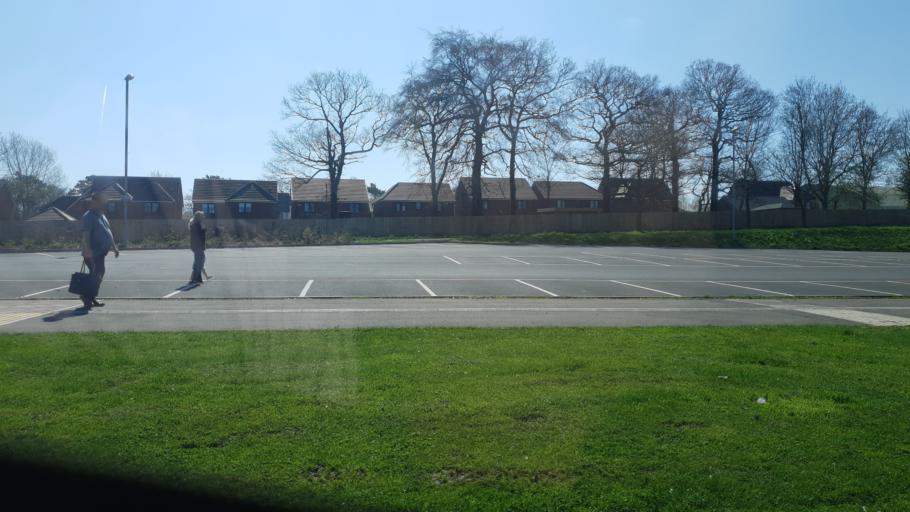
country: GB
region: England
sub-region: Middlesbrough
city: Nunthorpe
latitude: 54.5439
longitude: -1.2085
